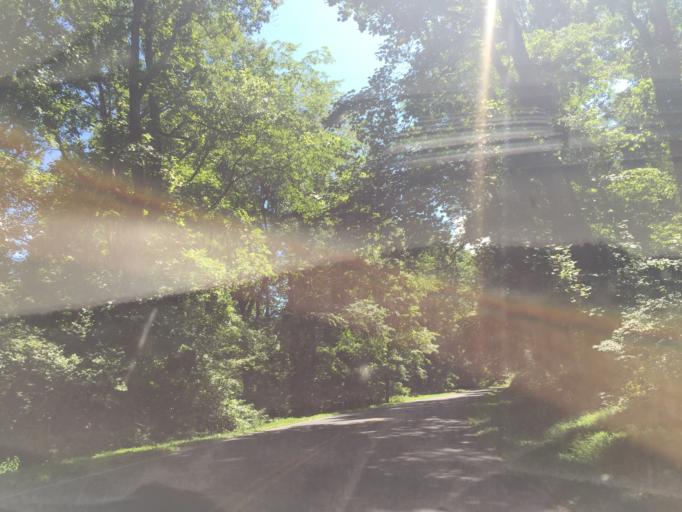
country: US
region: Virginia
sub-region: Warren County
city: Front Royal
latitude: 38.8411
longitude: -78.1842
